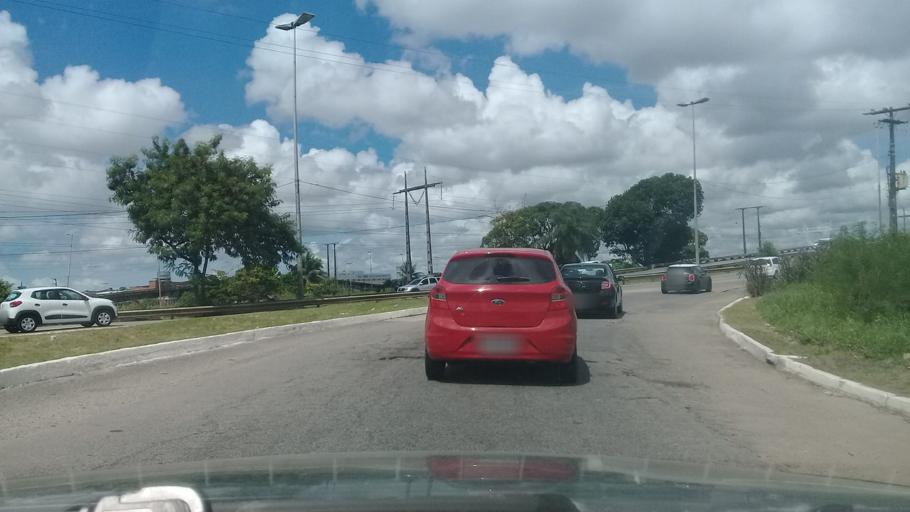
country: BR
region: Pernambuco
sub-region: Recife
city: Recife
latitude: -8.0657
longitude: -34.9404
